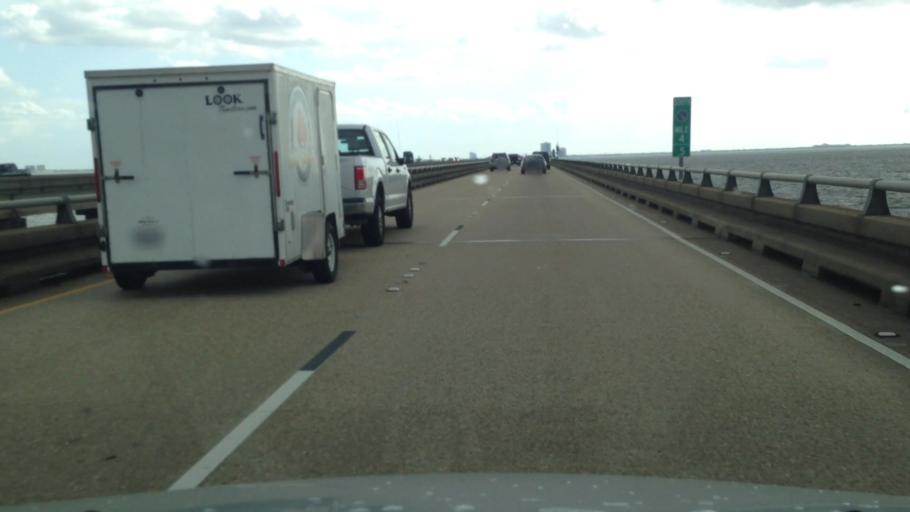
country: US
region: Louisiana
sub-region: Jefferson Parish
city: Metairie
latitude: 30.0865
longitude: -90.1428
